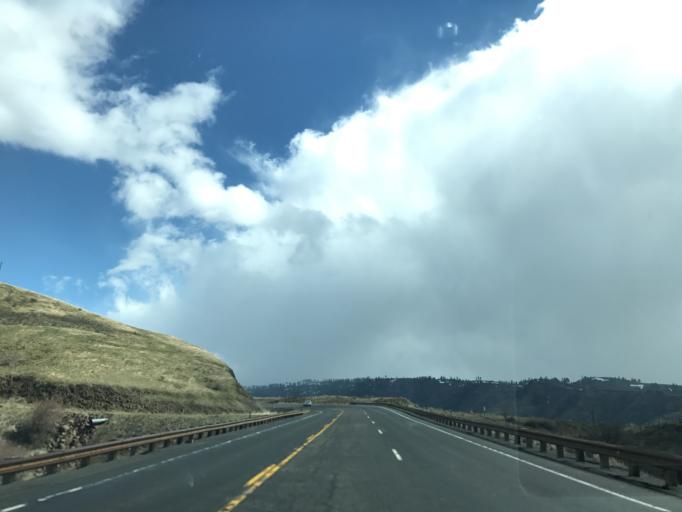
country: US
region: Idaho
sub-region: Idaho County
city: Grangeville
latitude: 45.8286
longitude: -116.2490
